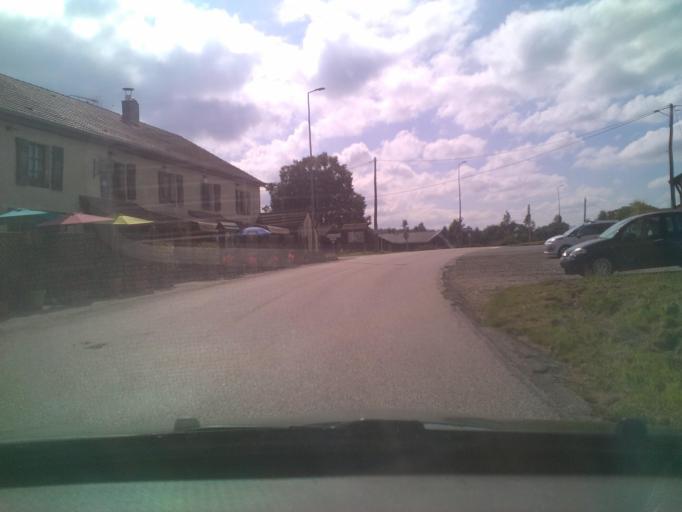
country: FR
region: Lorraine
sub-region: Departement des Vosges
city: Corcieux
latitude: 48.1484
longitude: 6.8649
